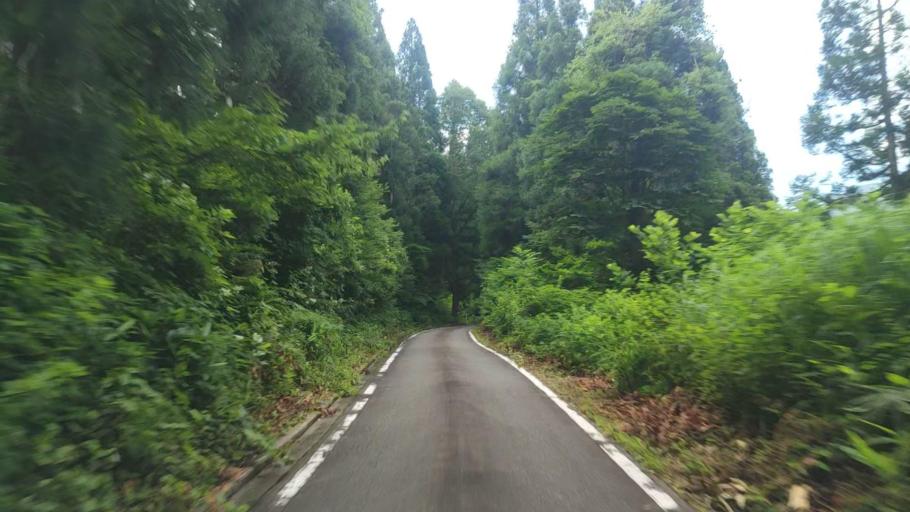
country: JP
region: Fukui
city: Katsuyama
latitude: 36.1703
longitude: 136.5239
